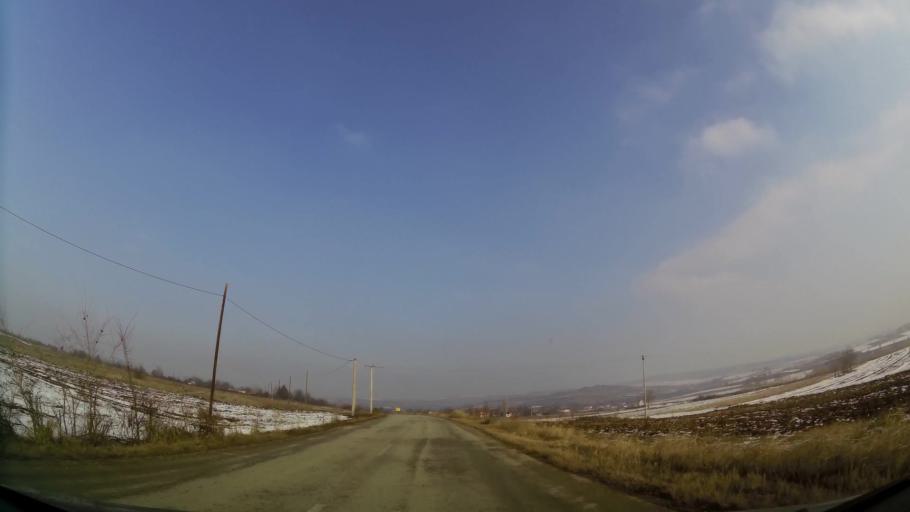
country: MK
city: Miladinovci
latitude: 41.9734
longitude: 21.6388
